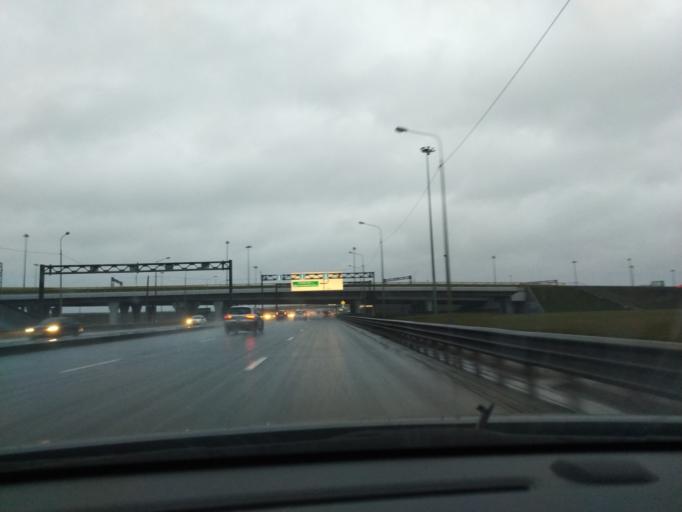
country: RU
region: St.-Petersburg
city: Sosnovaya Polyana
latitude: 59.7980
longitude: 30.1547
